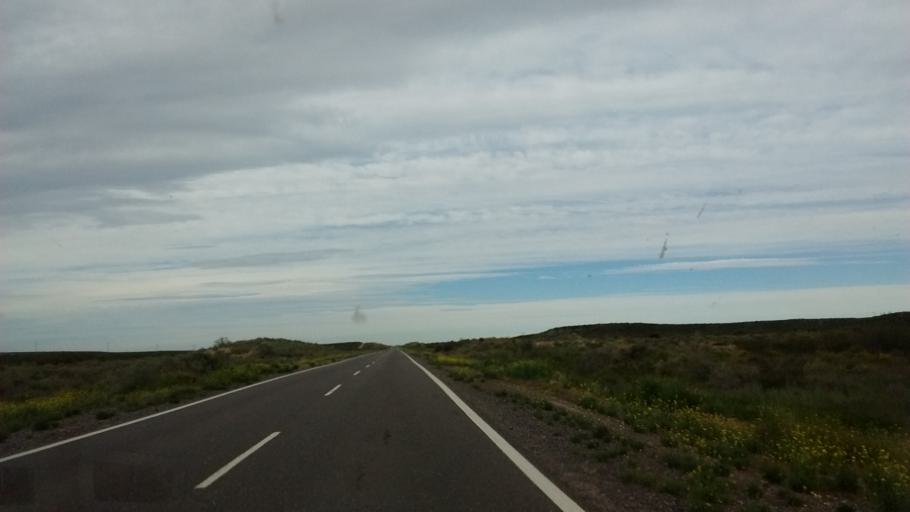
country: AR
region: Rio Negro
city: Contraalmirante Cordero
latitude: -38.4523
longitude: -68.0441
